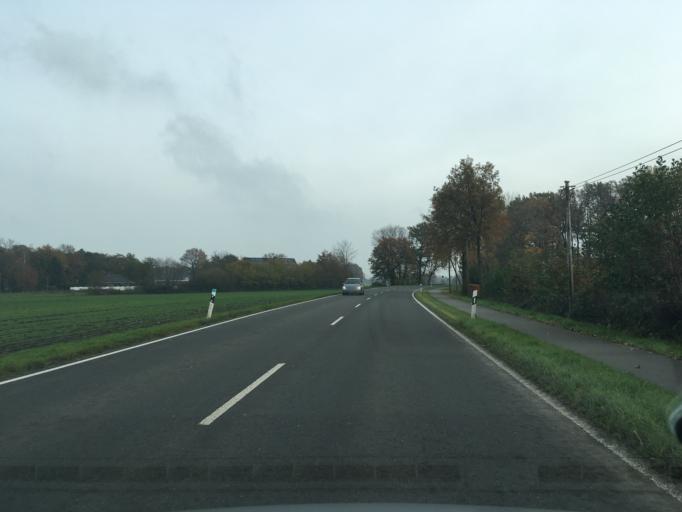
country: DE
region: North Rhine-Westphalia
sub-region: Regierungsbezirk Munster
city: Sudlohn
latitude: 51.9547
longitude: 6.8517
